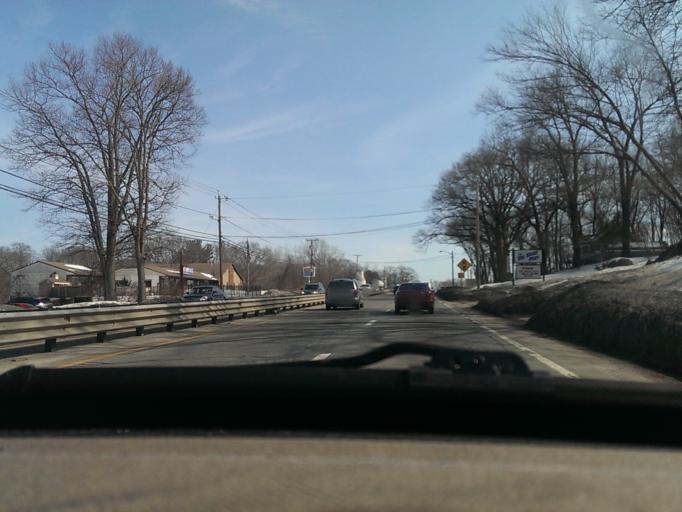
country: US
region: Rhode Island
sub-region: Providence County
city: Cumberland Hill
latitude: 41.9644
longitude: -71.4985
